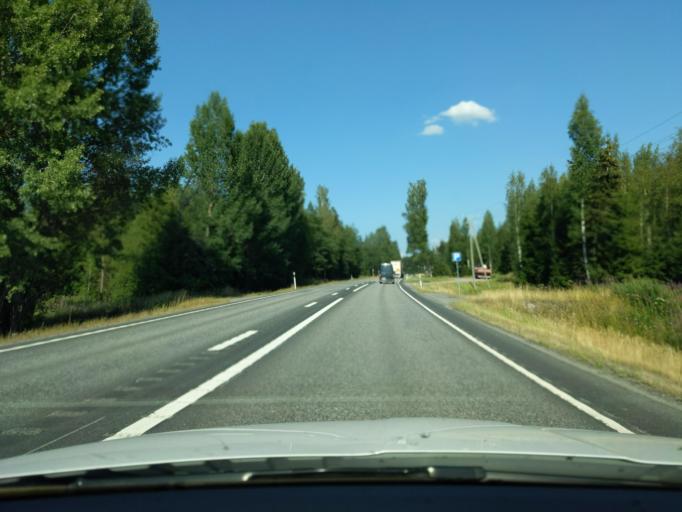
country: FI
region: Paijanne Tavastia
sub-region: Lahti
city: Hollola
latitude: 60.9379
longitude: 25.3938
